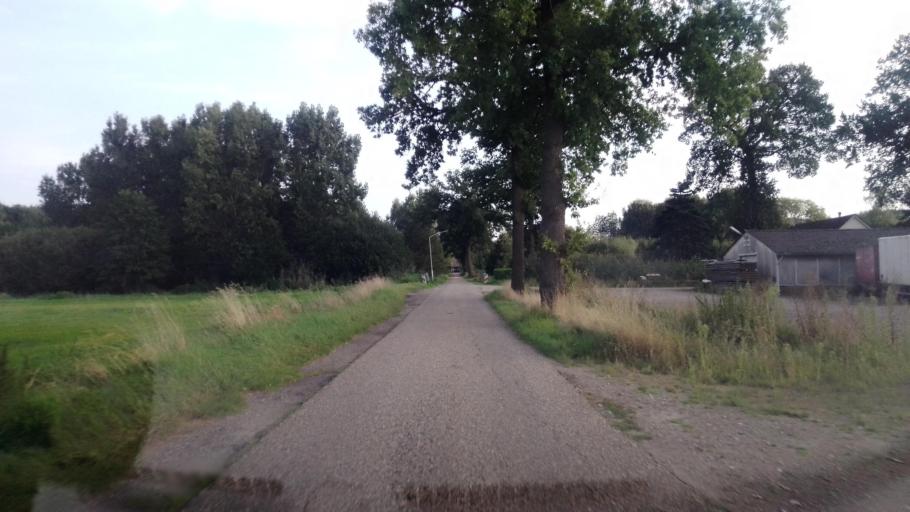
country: NL
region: Limburg
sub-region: Gemeente Peel en Maas
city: Maasbree
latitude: 51.3893
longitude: 5.9257
